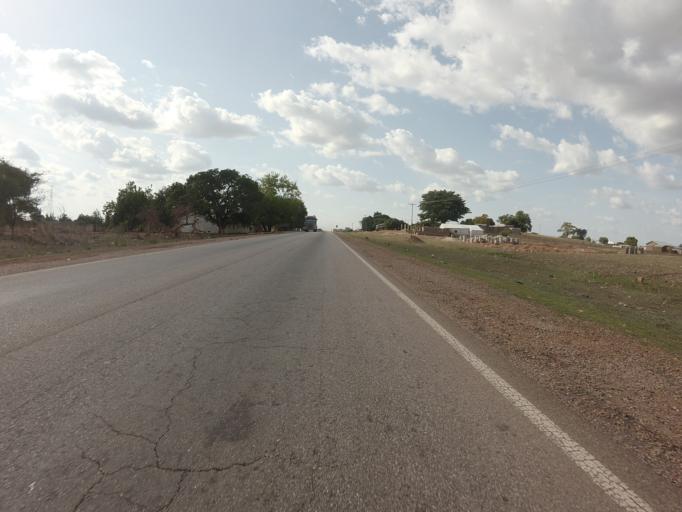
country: GH
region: Upper East
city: Bolgatanga
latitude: 10.6782
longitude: -0.8618
